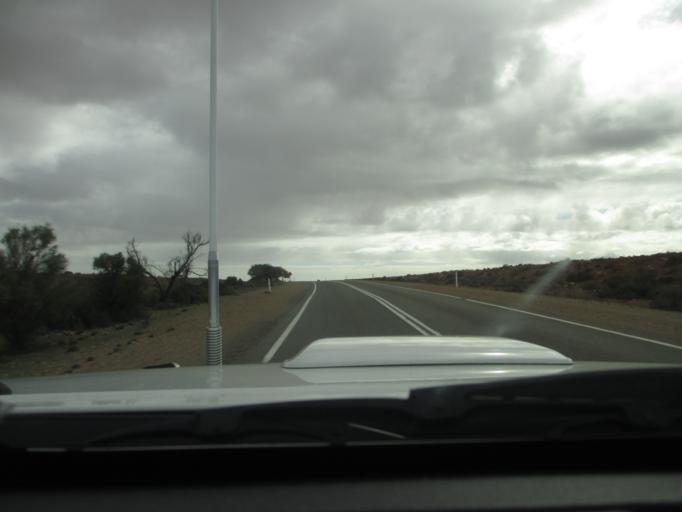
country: AU
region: South Australia
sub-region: Flinders Ranges
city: Quorn
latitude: -31.5587
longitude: 138.4288
